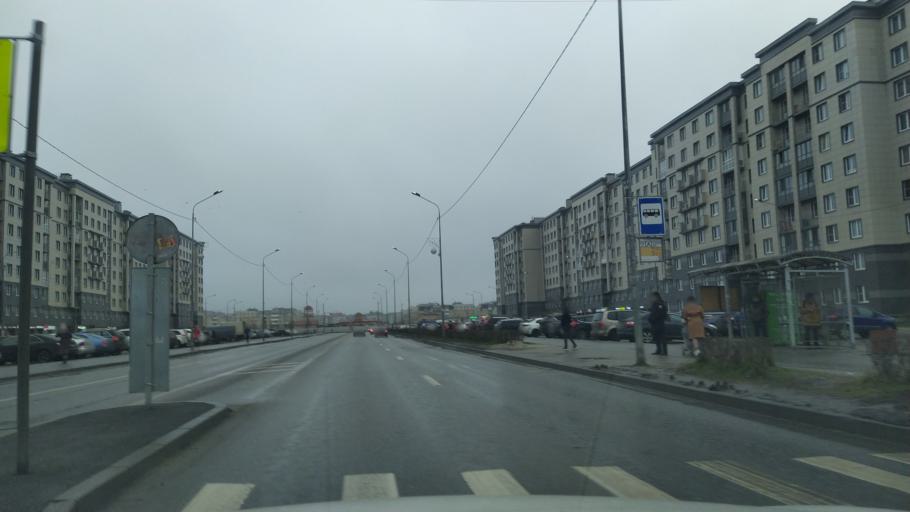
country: RU
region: St.-Petersburg
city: Tyarlevo
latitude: 59.7399
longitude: 30.4695
